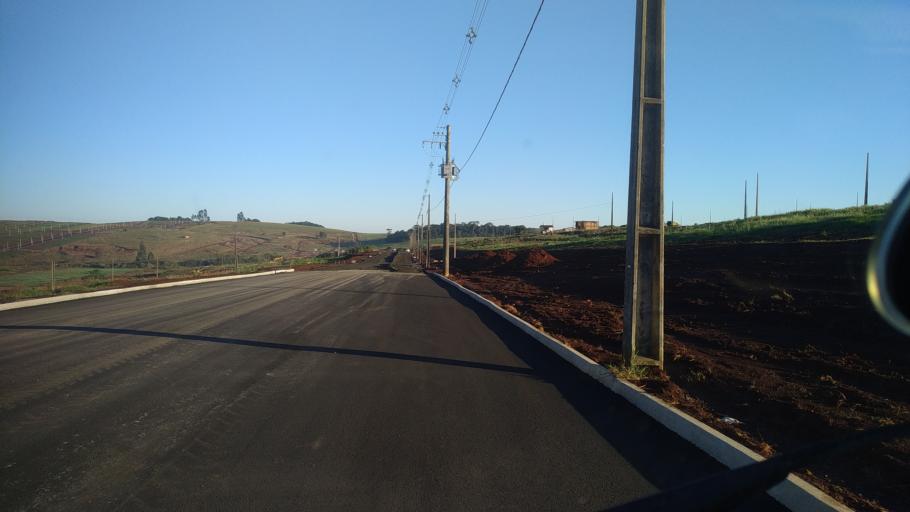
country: BR
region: Santa Catarina
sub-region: Chapeco
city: Chapeco
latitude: -27.0888
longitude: -52.6953
